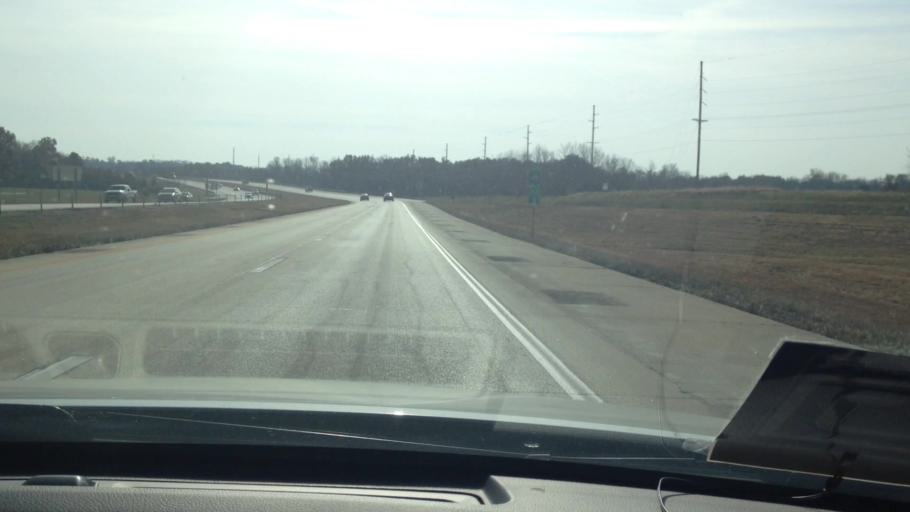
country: US
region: Missouri
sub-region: Cass County
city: Harrisonville
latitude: 38.6514
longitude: -94.3655
